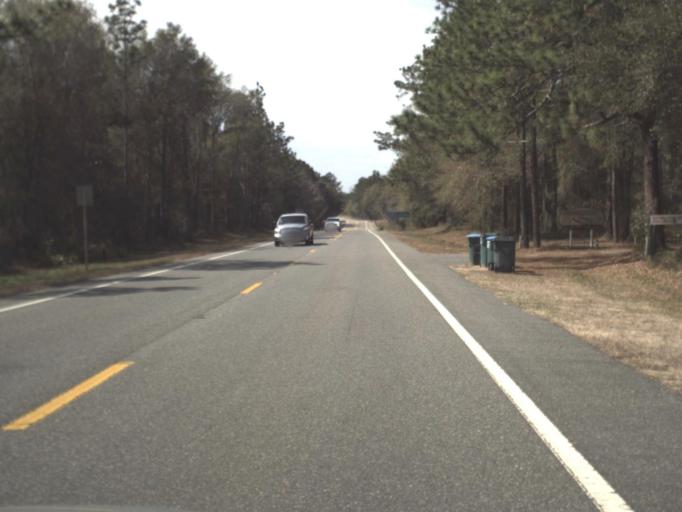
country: US
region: Florida
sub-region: Gadsden County
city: Gretna
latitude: 30.5213
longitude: -84.8138
